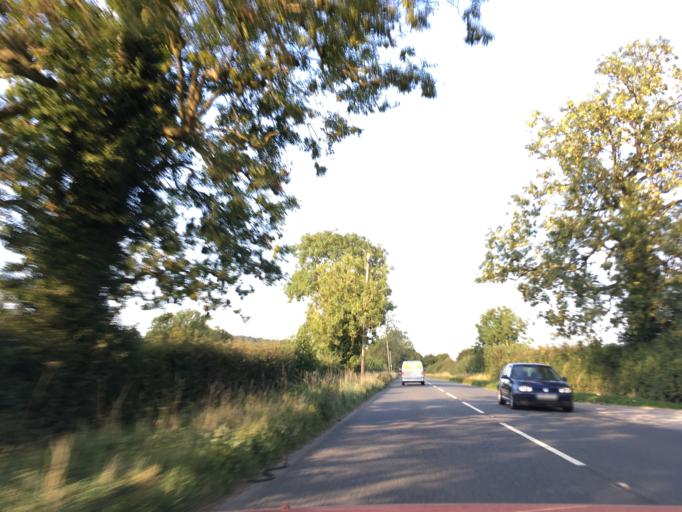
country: GB
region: England
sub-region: Gloucestershire
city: Stow on the Wold
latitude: 51.9067
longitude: -1.7397
